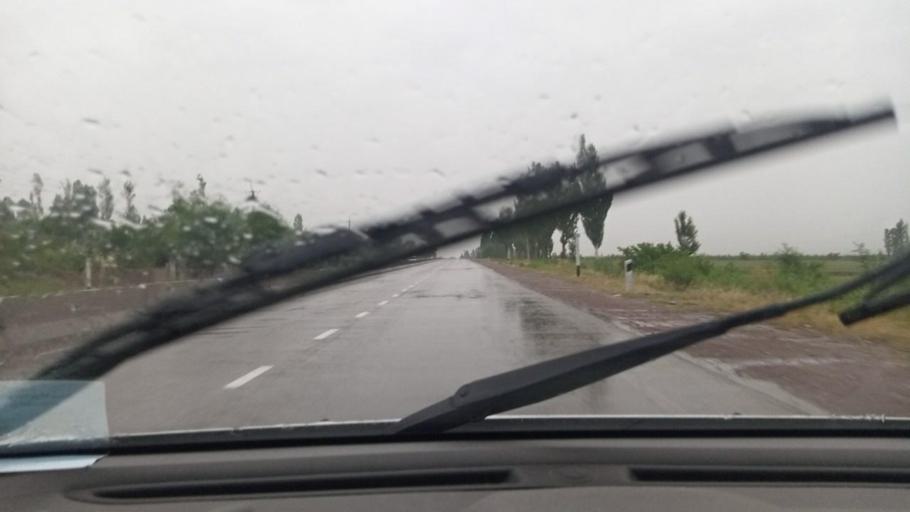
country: UZ
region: Toshkent
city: Angren
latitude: 40.9657
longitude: 69.9615
